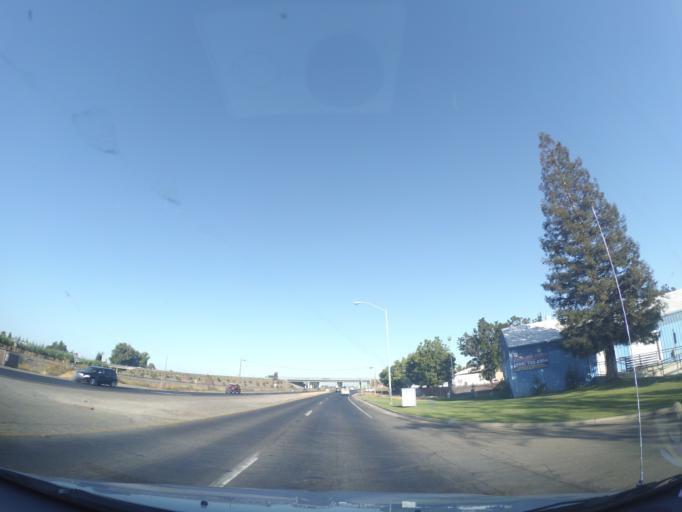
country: US
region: California
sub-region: Merced County
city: Merced
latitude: 37.3088
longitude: -120.5075
